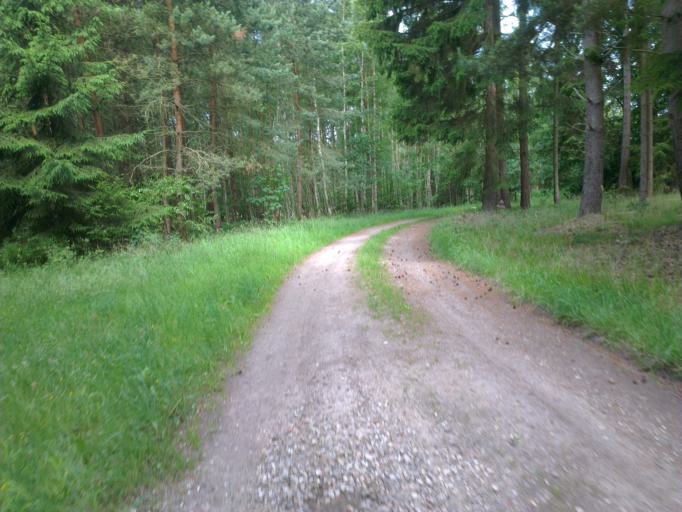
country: DK
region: Capital Region
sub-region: Frederikssund Kommune
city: Jaegerspris
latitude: 55.9035
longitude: 12.0146
